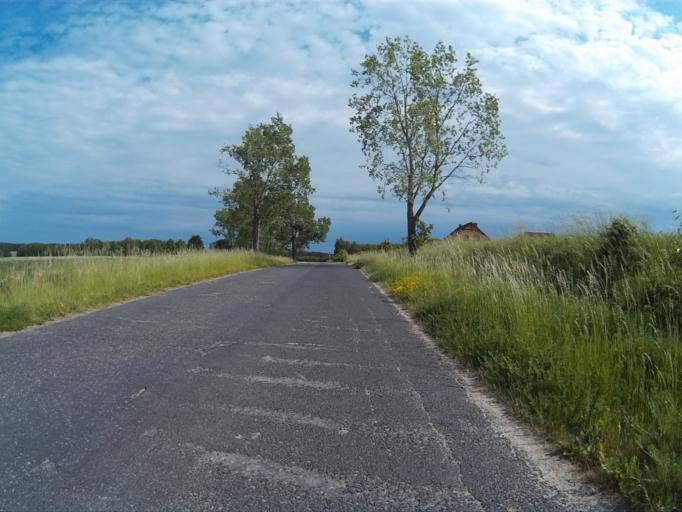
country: PL
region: Kujawsko-Pomorskie
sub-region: Powiat tucholski
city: Lubiewo
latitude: 53.4809
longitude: 17.9488
